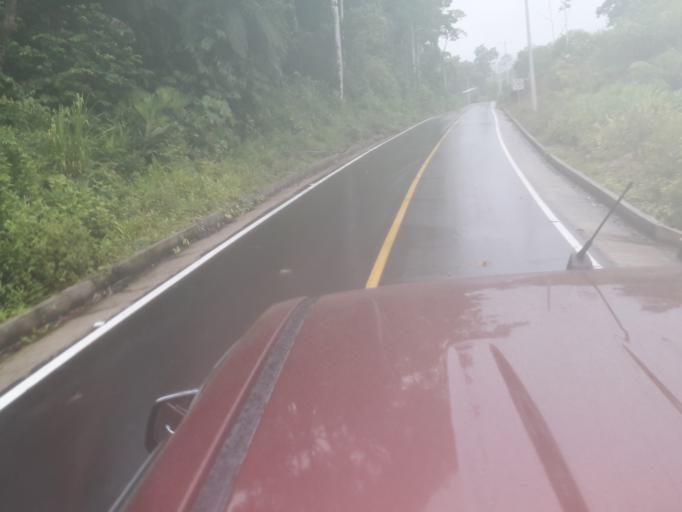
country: EC
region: Napo
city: Tena
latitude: -1.0241
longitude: -77.6648
